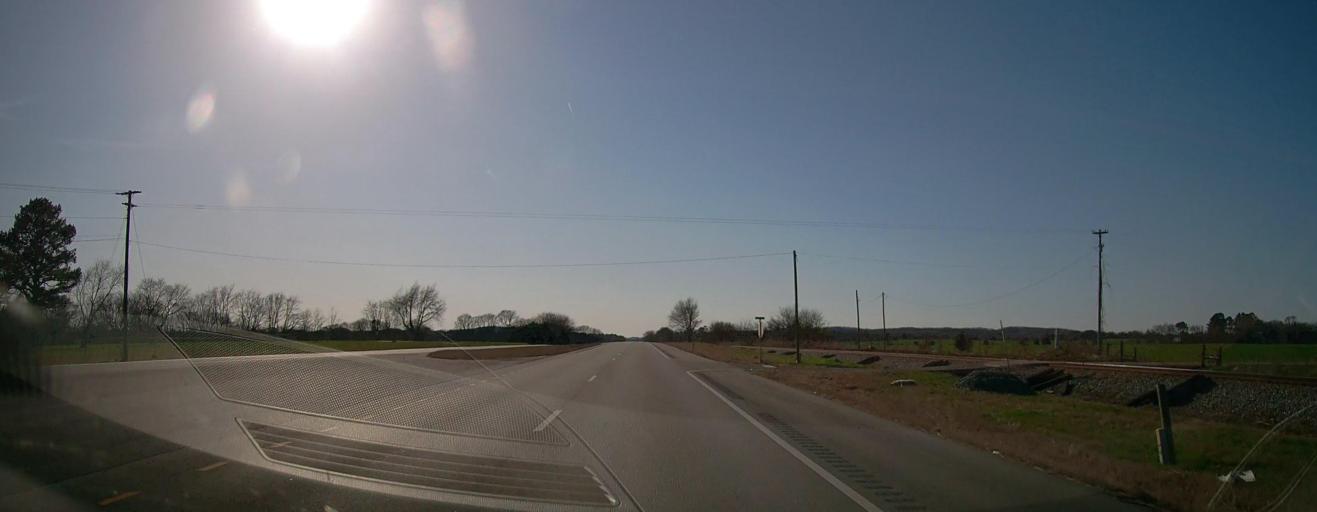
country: US
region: Alabama
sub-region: Colbert County
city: Cherokee
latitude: 34.7590
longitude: -87.9927
